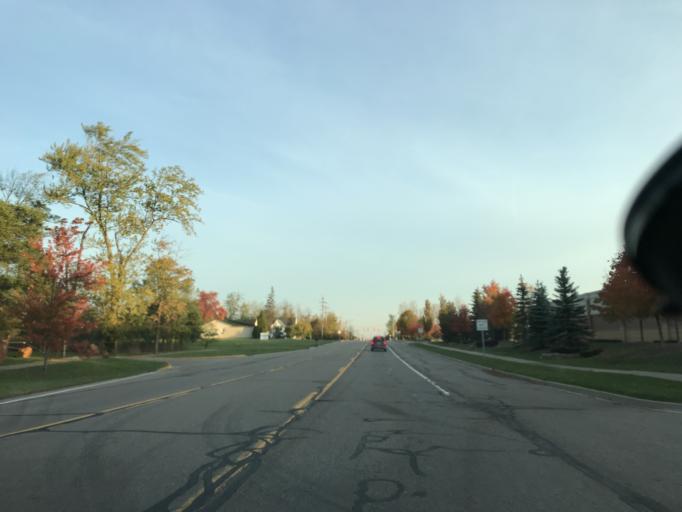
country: US
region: Michigan
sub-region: Oakland County
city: Wixom
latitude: 42.4868
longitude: -83.5352
